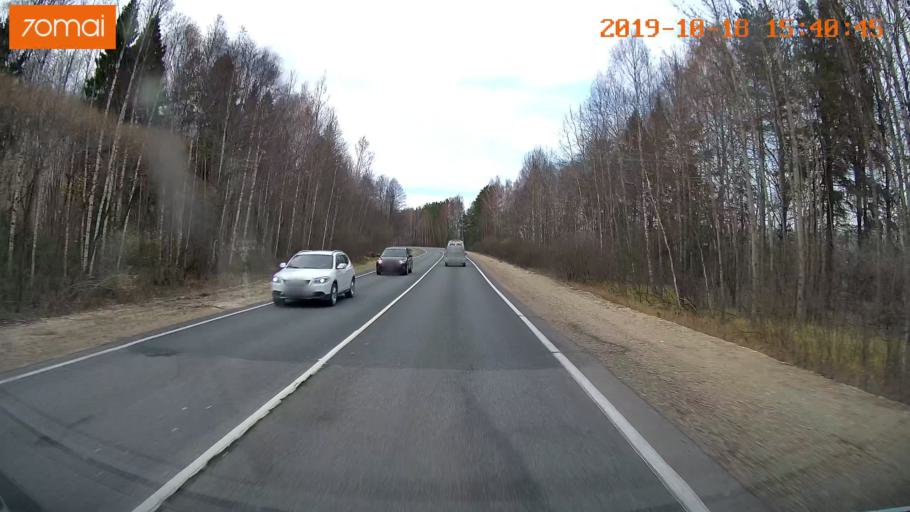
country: RU
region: Vladimir
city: Golovino
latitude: 55.9381
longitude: 40.5918
